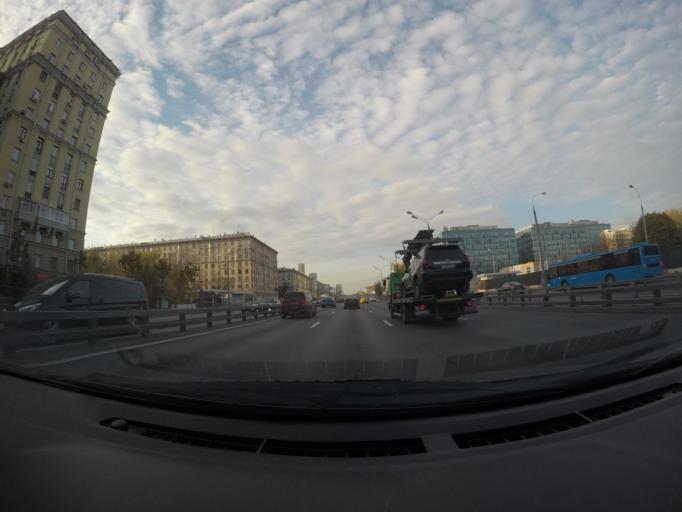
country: RU
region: Moskovskaya
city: Koptevo
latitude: 55.8192
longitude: 37.4978
